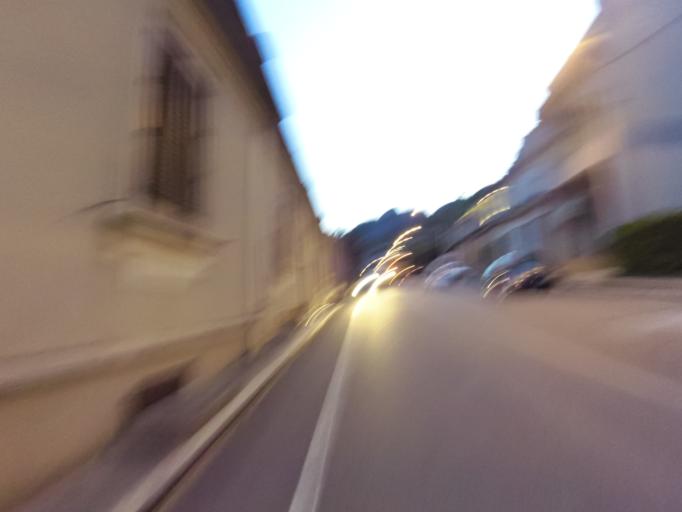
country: IT
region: Calabria
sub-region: Provincia di Reggio Calabria
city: Stilo
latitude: 38.4762
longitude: 16.4662
